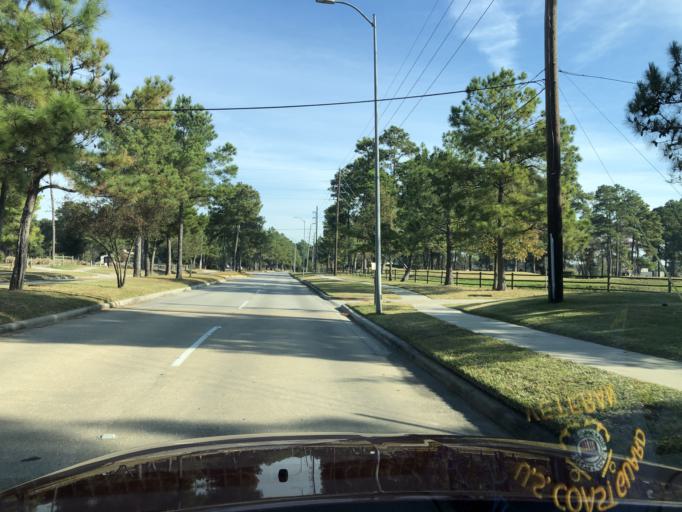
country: US
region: Texas
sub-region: Harris County
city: Tomball
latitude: 30.0348
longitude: -95.5638
